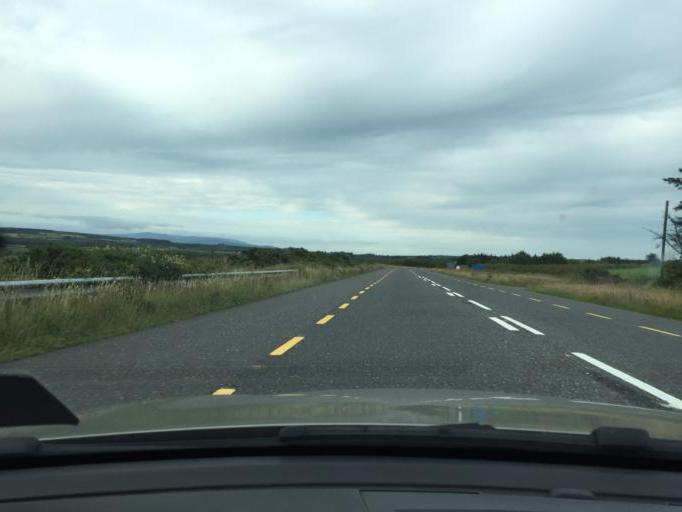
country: IE
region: Munster
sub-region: Waterford
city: Dungarvan
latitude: 52.0128
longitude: -7.7009
